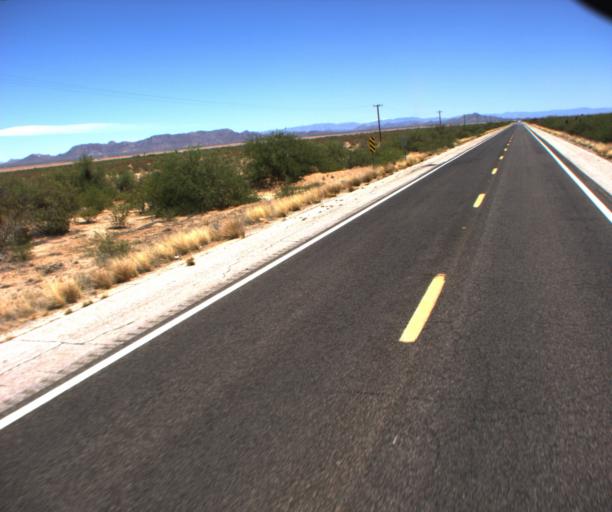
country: US
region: Arizona
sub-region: La Paz County
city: Salome
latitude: 33.9232
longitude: -113.2398
